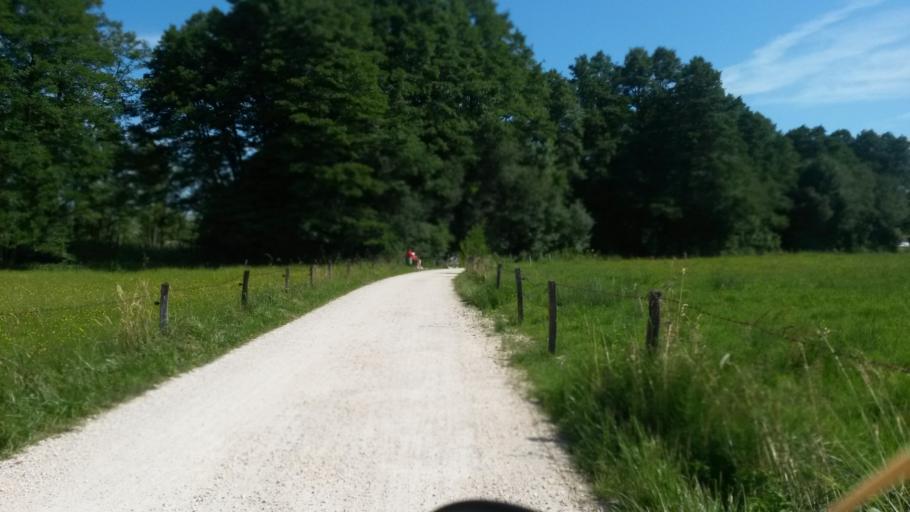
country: DE
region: Bavaria
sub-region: Upper Bavaria
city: Chiemsee
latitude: 47.8327
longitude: 12.4168
